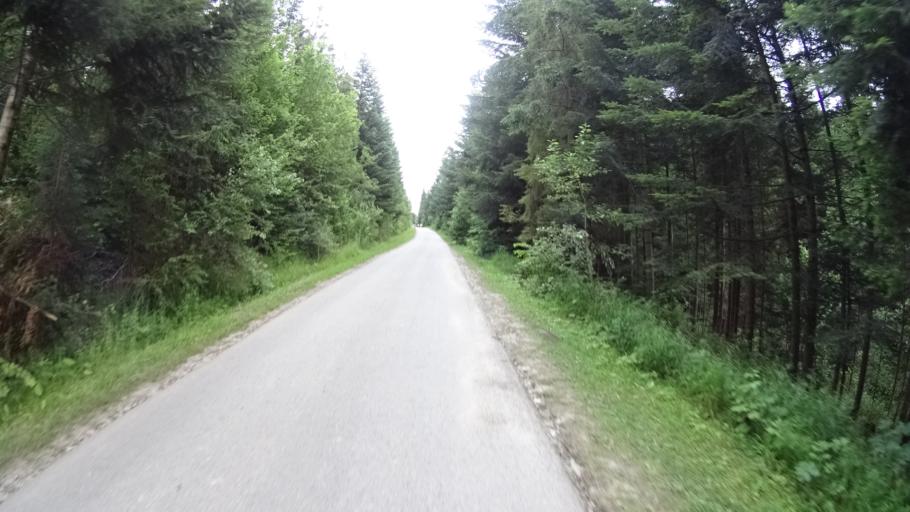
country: PL
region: Lesser Poland Voivodeship
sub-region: Powiat nowotarski
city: Krosnica
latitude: 49.4398
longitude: 20.3235
